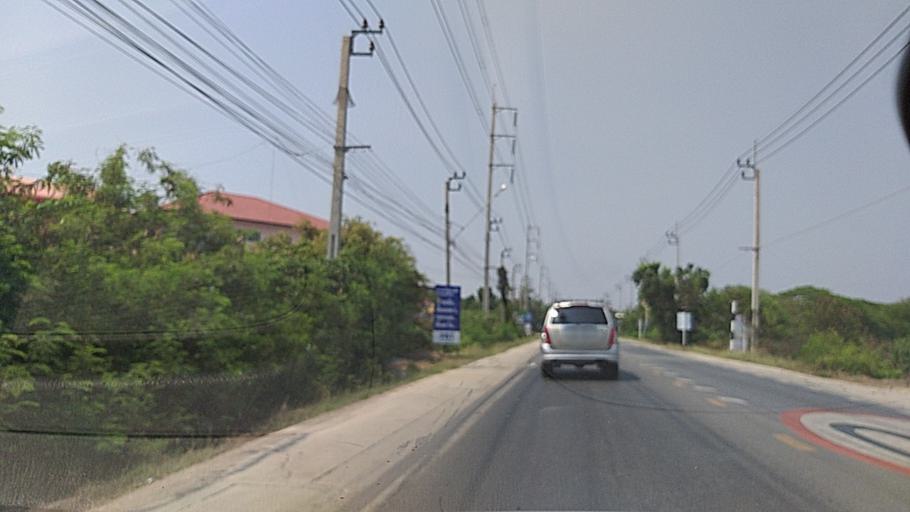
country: TH
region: Nonthaburi
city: Sai Noi
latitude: 13.9724
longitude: 100.3102
